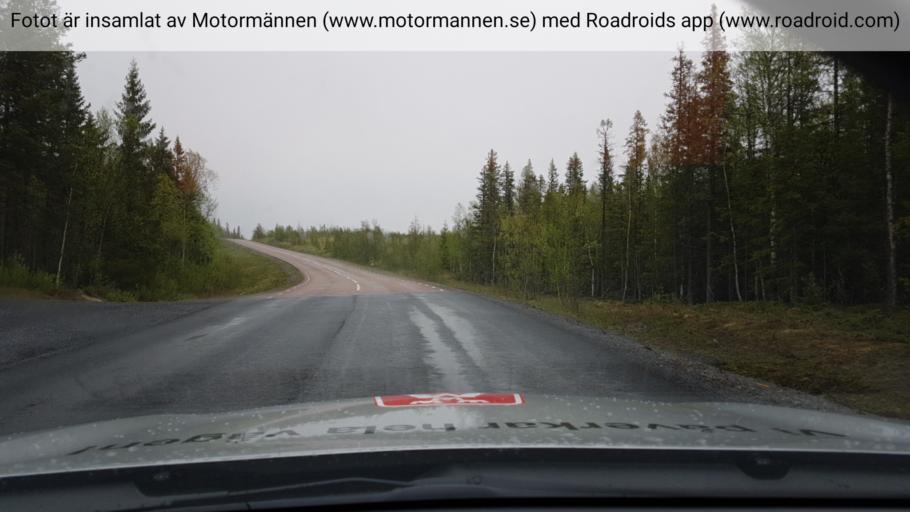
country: SE
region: Jaemtland
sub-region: Krokoms Kommun
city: Valla
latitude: 63.1143
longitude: 13.9098
